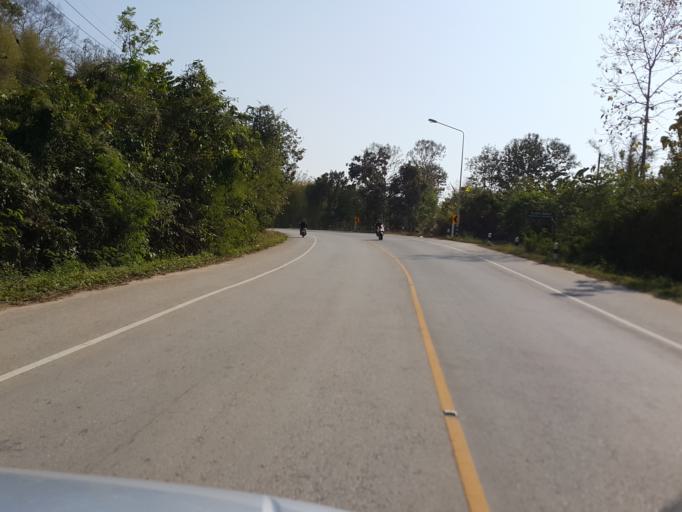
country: TH
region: Lampang
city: Chae Hom
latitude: 18.7692
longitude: 99.5727
